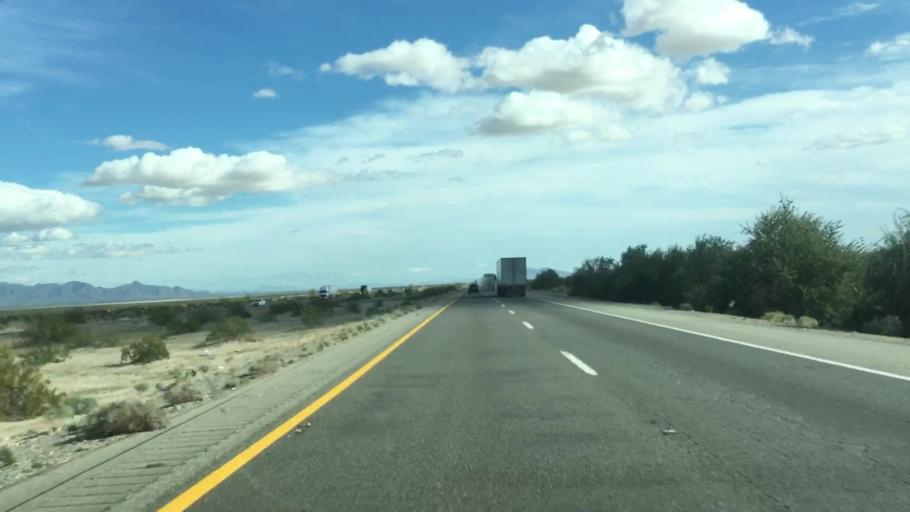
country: US
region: California
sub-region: Riverside County
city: Mesa Verde
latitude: 33.6474
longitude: -115.1256
